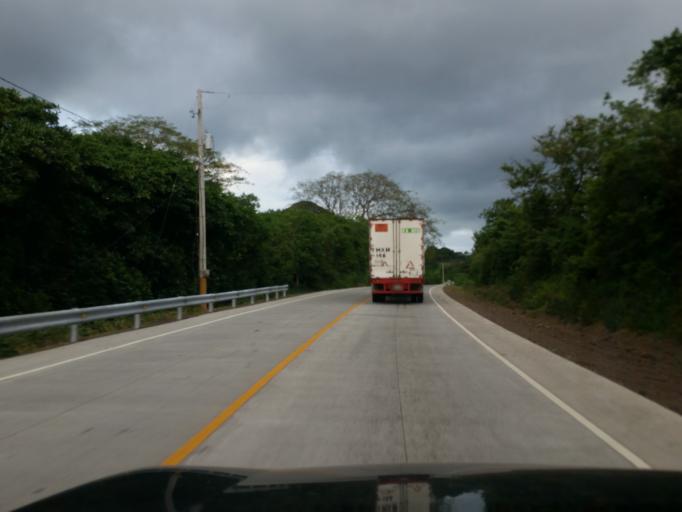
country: NI
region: Managua
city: Ciudad Sandino
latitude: 12.0831
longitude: -86.3947
